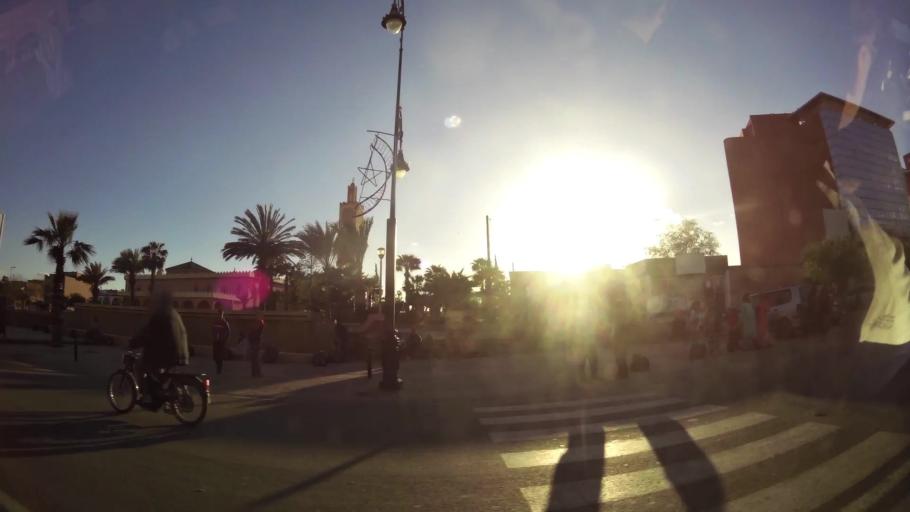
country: MA
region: Marrakech-Tensift-Al Haouz
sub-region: Kelaa-Des-Sraghna
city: Sidi Abdallah
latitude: 32.2361
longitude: -7.9586
